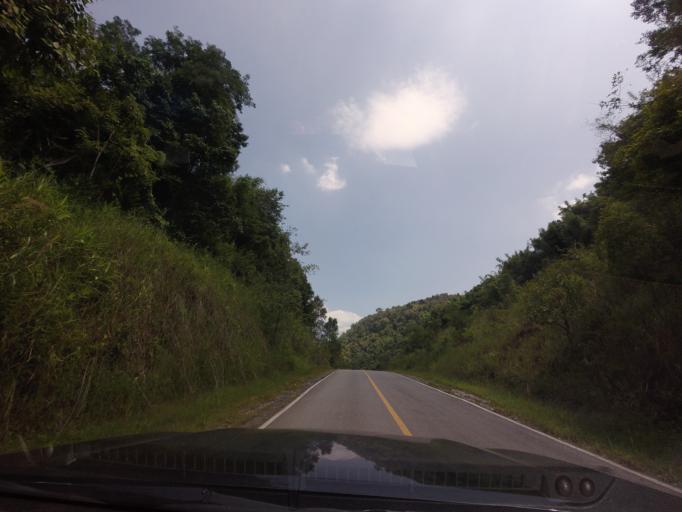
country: TH
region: Loei
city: Na Haeo
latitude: 17.6249
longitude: 100.9031
